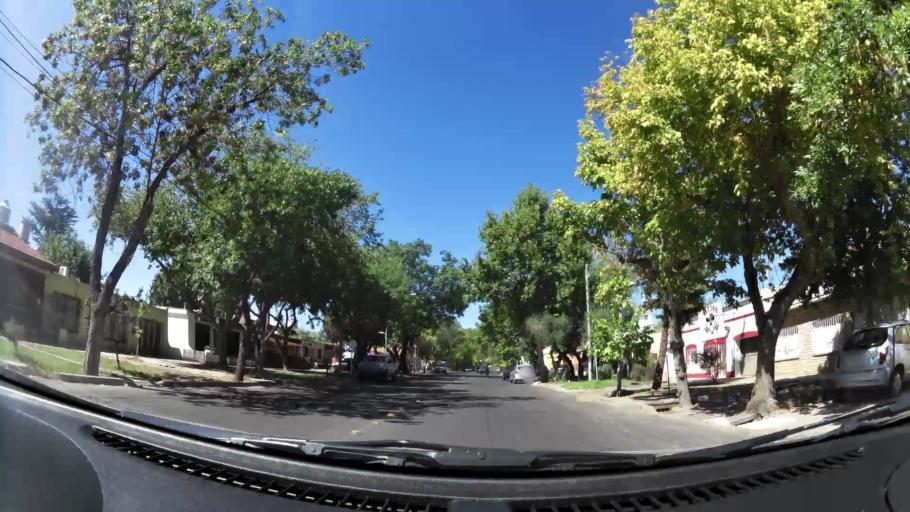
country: AR
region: Mendoza
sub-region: Departamento de Godoy Cruz
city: Godoy Cruz
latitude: -32.9174
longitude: -68.8594
